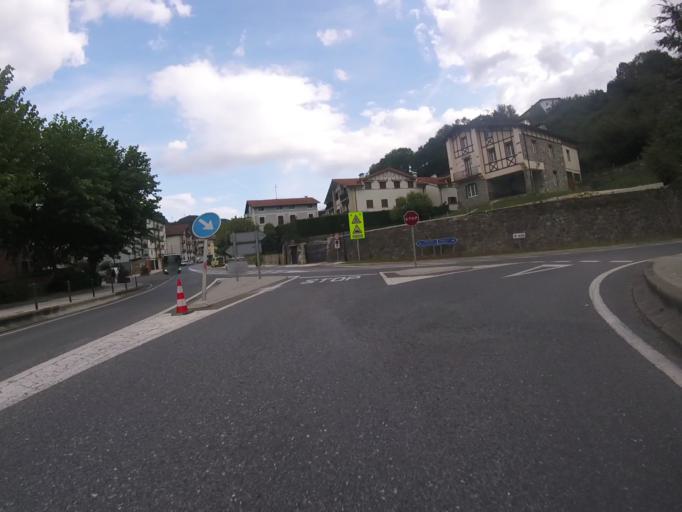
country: ES
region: Basque Country
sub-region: Provincia de Guipuzcoa
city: Anoeta
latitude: 43.1642
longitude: -2.0695
